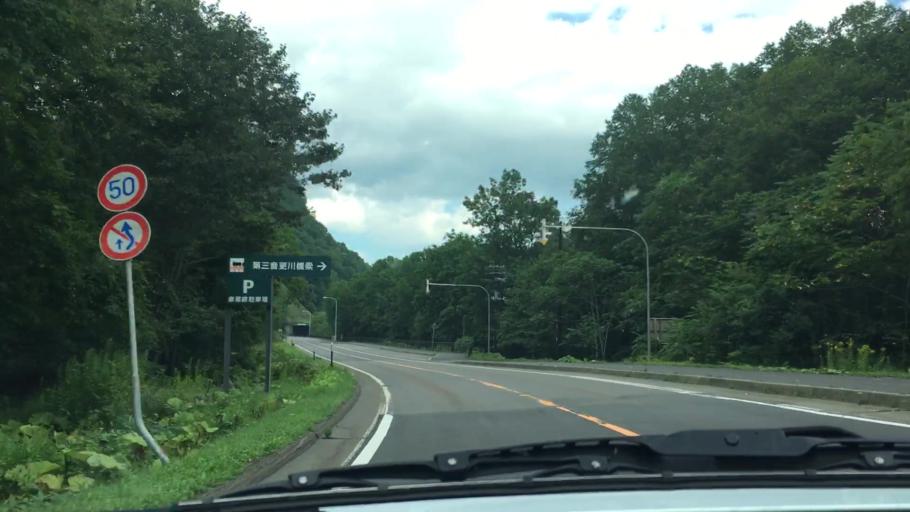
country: JP
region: Hokkaido
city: Otofuke
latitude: 43.3563
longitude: 143.2560
